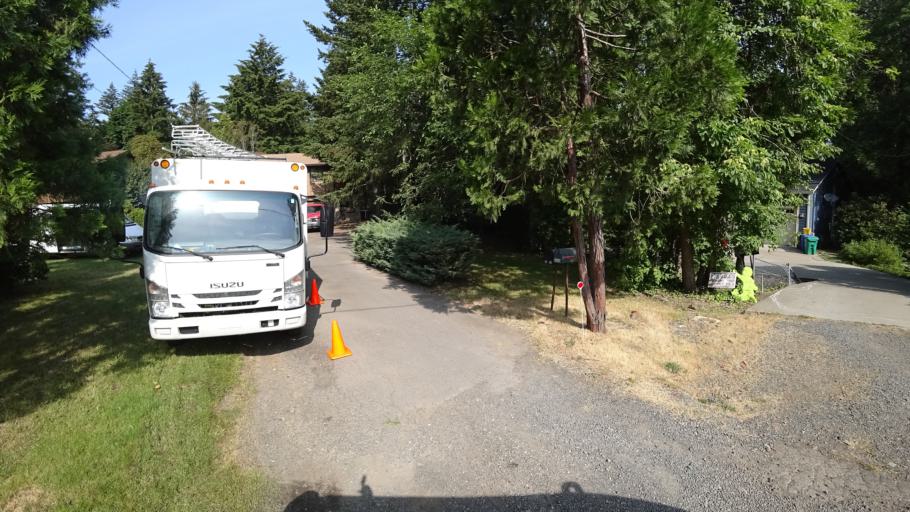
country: US
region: Oregon
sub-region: Washington County
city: Garden Home-Whitford
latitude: 45.4593
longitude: -122.7167
